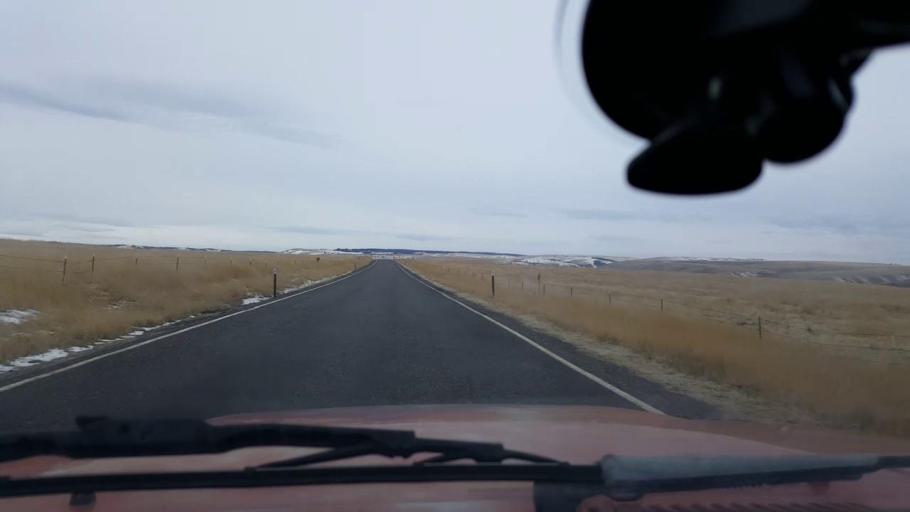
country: US
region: Washington
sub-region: Asotin County
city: Clarkston Heights-Vineland
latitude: 46.3136
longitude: -117.3335
